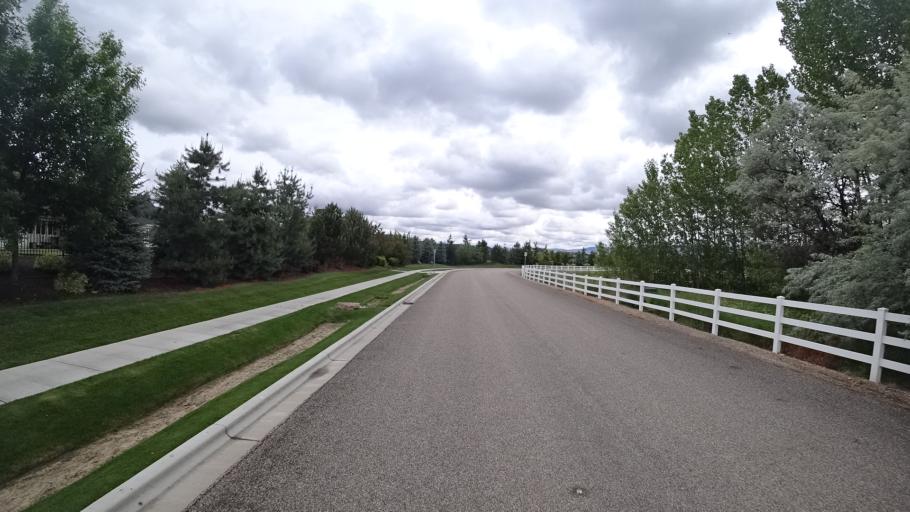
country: US
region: Idaho
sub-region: Ada County
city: Eagle
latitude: 43.6853
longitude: -116.3715
